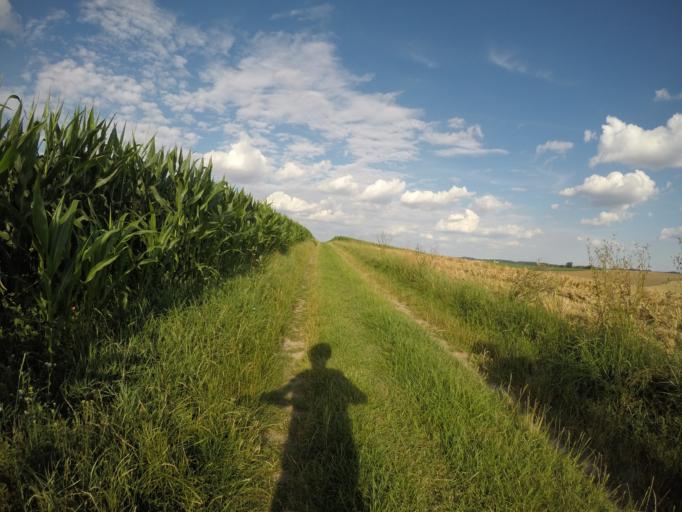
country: DE
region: Bavaria
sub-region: Lower Bavaria
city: Tiefenbach
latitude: 48.5079
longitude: 12.1174
